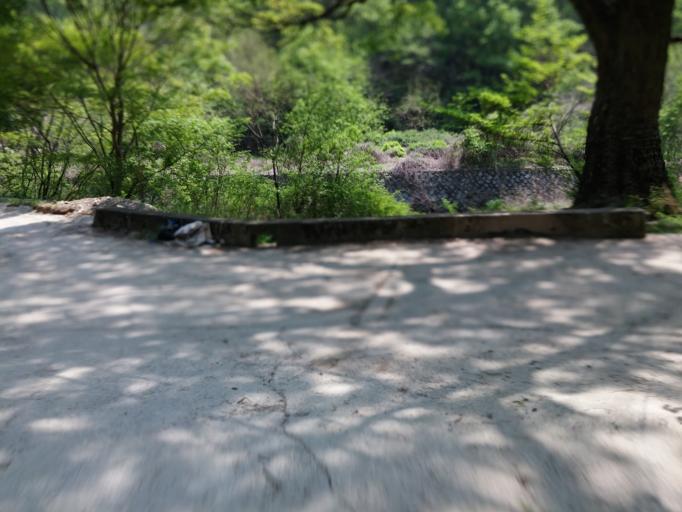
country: KR
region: Chungcheongbuk-do
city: Okcheon
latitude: 36.4121
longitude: 127.5980
